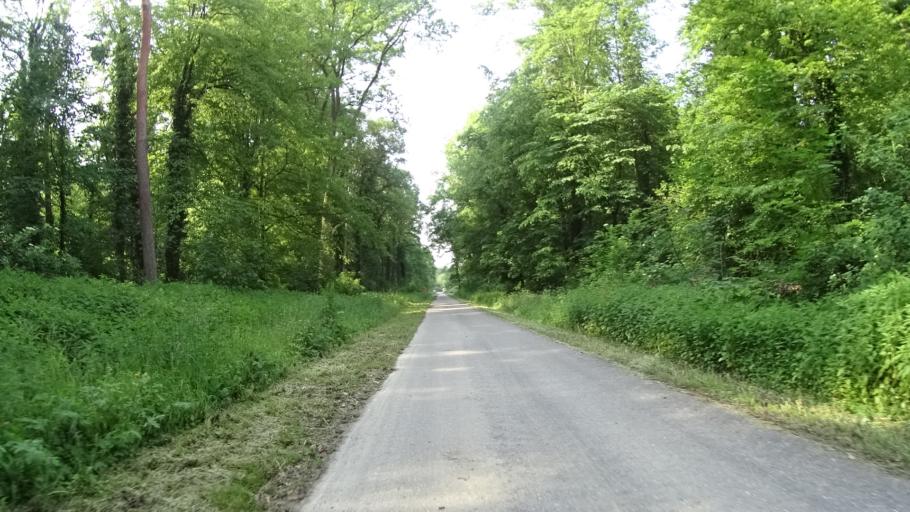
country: DE
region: Baden-Wuerttemberg
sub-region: Karlsruhe Region
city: Walldorf
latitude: 49.3300
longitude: 8.6230
